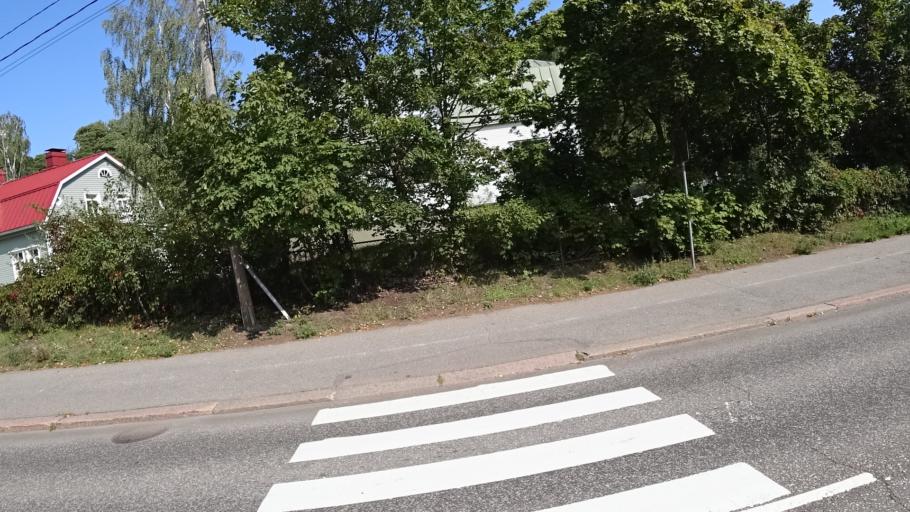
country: FI
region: Kymenlaakso
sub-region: Kotka-Hamina
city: Kotka
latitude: 60.4599
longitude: 26.9268
